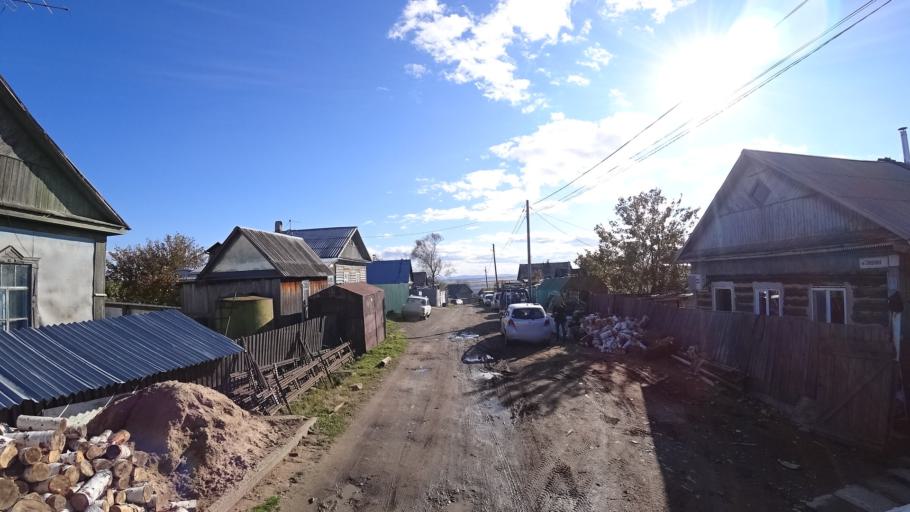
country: RU
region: Khabarovsk Krai
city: Amursk
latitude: 50.2344
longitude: 136.9212
